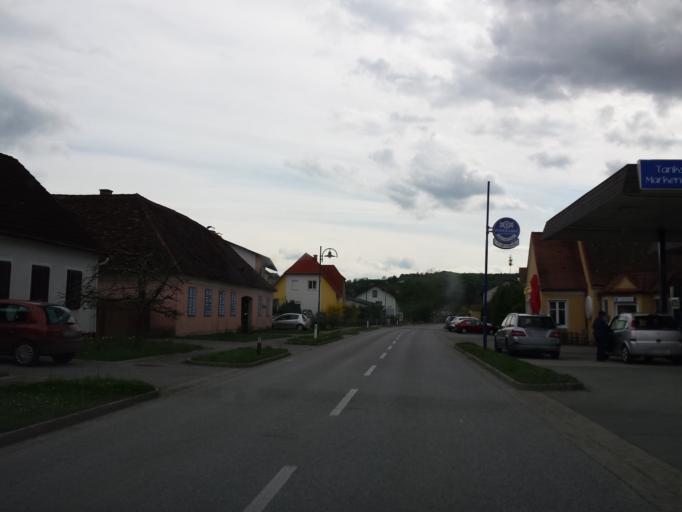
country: AT
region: Styria
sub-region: Politischer Bezirk Hartberg-Fuerstenfeld
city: UEbersbach
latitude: 47.0212
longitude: 16.0533
